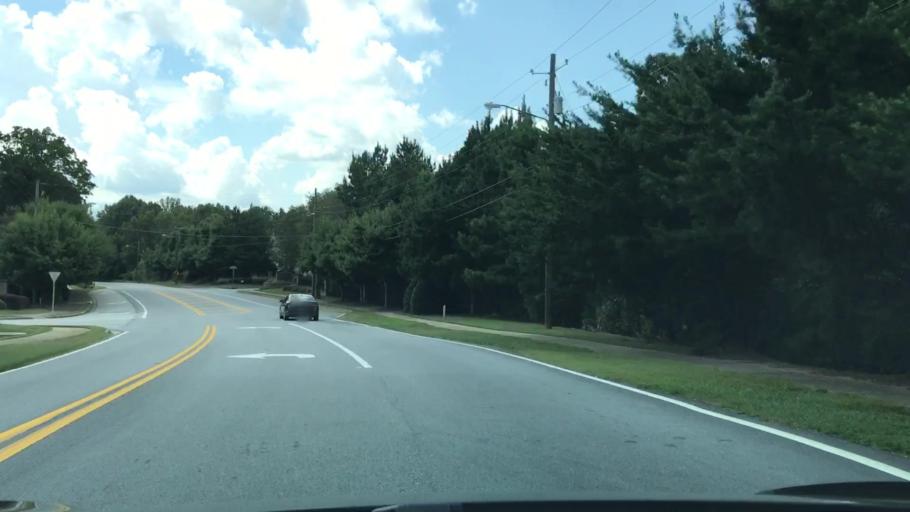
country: US
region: Georgia
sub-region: Gwinnett County
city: Snellville
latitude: 33.9052
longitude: -84.0683
